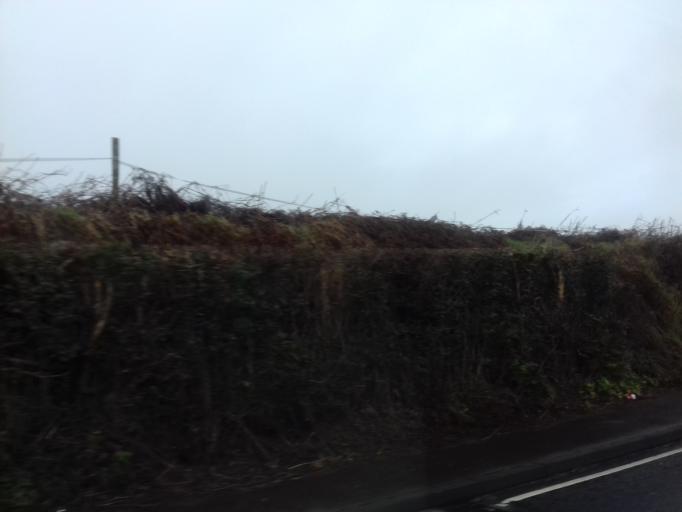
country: GB
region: Northern Ireland
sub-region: Strabane District
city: Sion Mills
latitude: 54.7740
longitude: -7.4660
